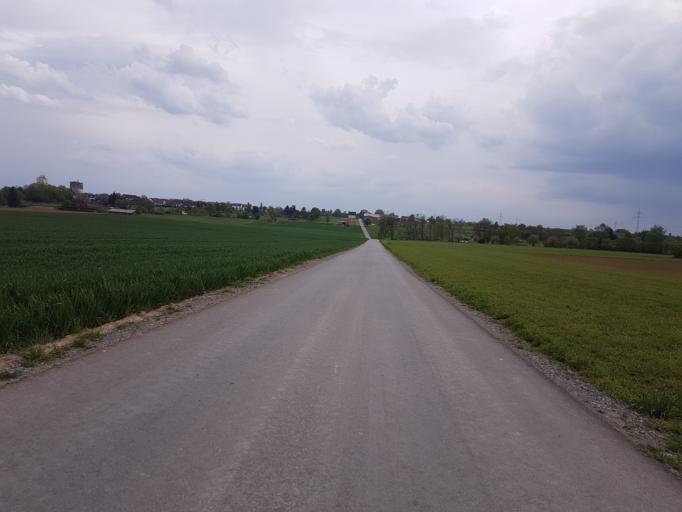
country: DE
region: Baden-Wuerttemberg
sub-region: Regierungsbezirk Stuttgart
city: Bondorf
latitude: 48.5297
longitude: 8.8220
